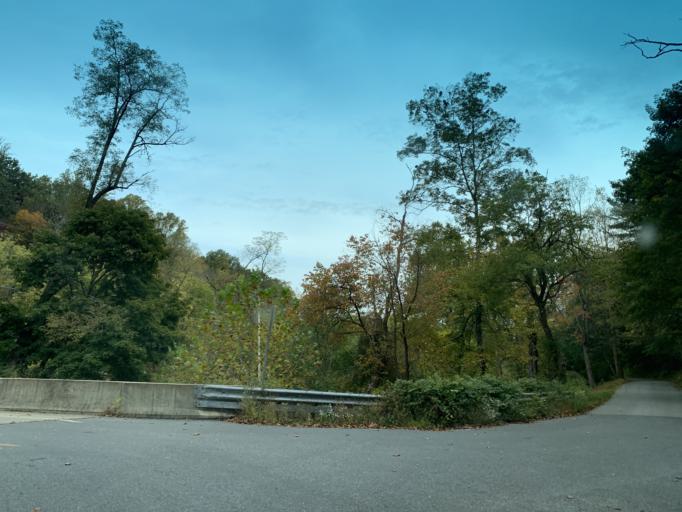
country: US
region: Pennsylvania
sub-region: York County
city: Stewartstown
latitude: 39.8254
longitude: -76.5104
